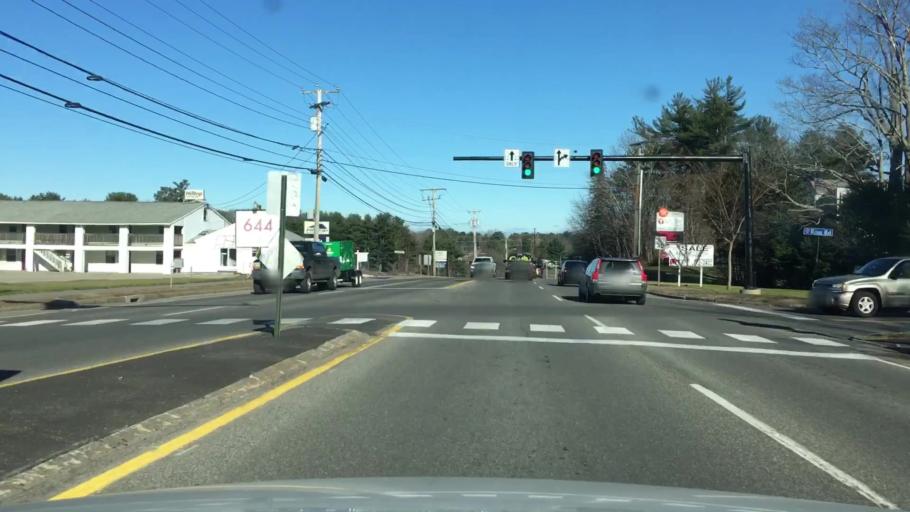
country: US
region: Maine
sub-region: York County
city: Saco
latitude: 43.5149
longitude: -70.4296
